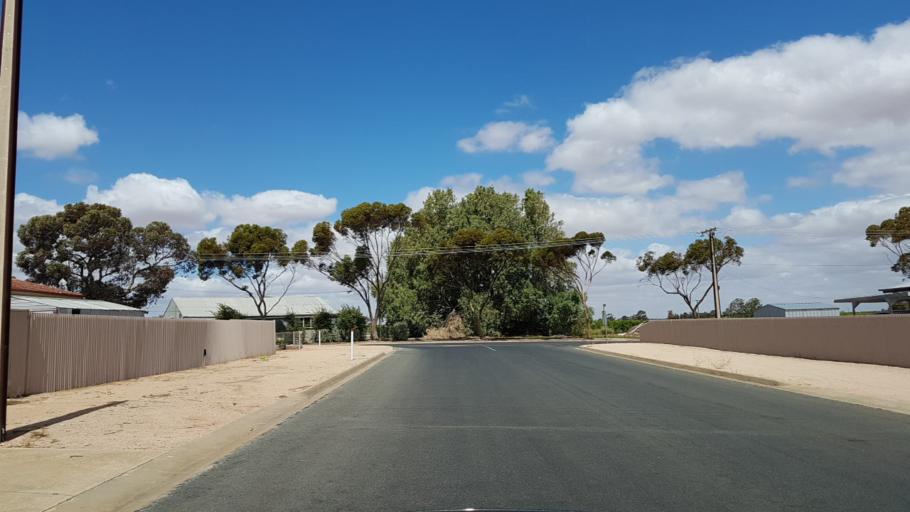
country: AU
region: South Australia
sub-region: Loxton Waikerie
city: Waikerie
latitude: -34.1839
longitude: 139.9909
